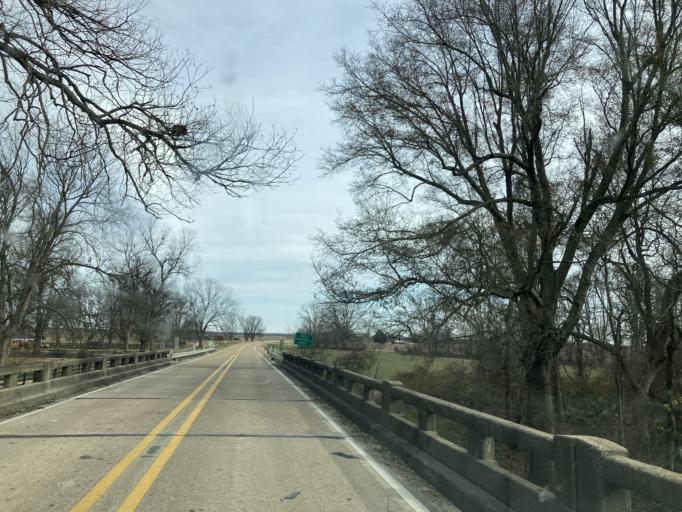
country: US
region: Mississippi
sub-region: Washington County
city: Hollandale
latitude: 33.1842
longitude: -90.6855
